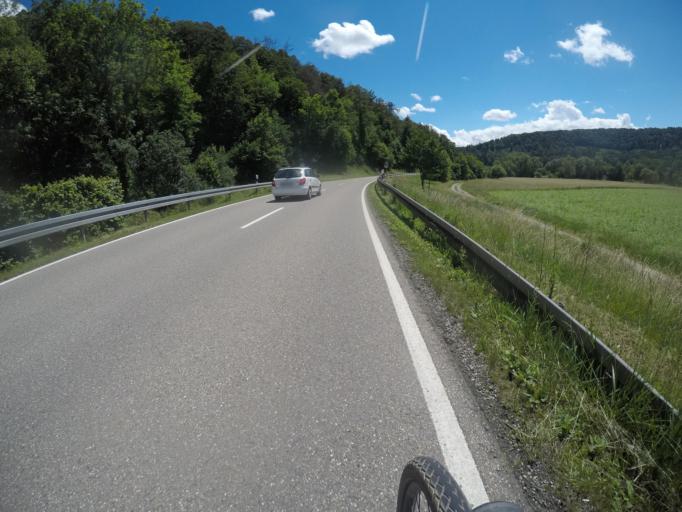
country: DE
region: Baden-Wuerttemberg
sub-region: Regierungsbezirk Stuttgart
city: Bondorf
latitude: 48.4484
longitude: 8.8152
